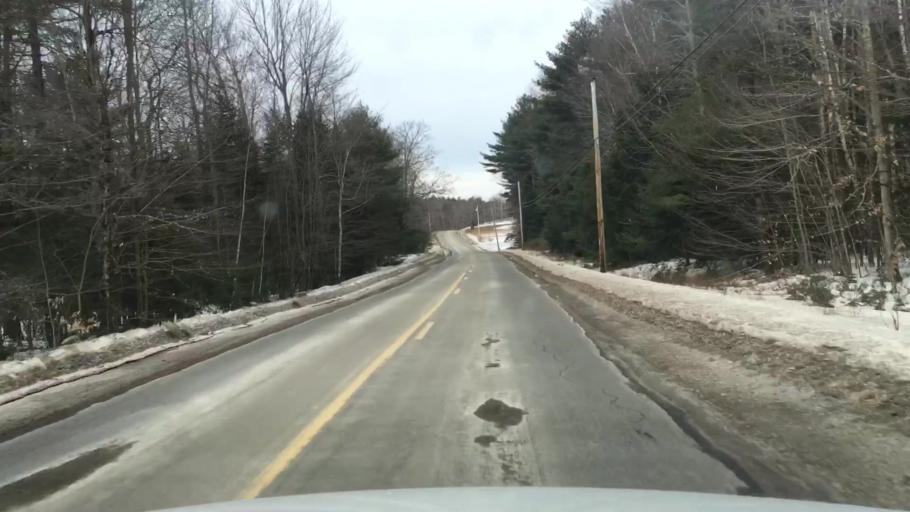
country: US
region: Maine
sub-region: Kennebec County
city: Chelsea
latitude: 44.2637
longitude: -69.6480
